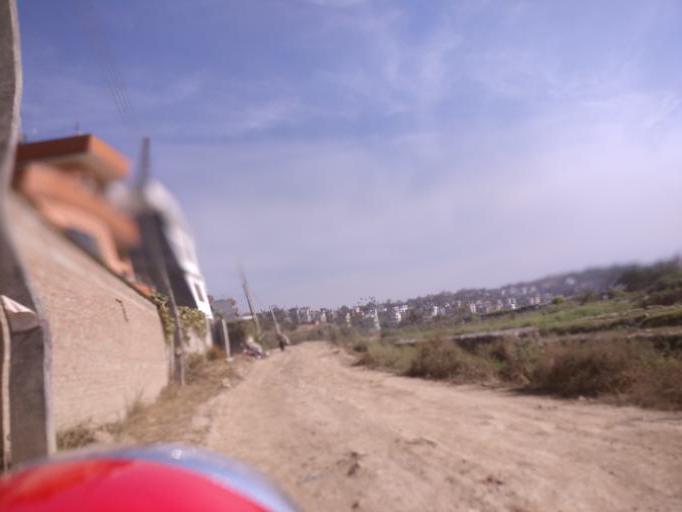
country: NP
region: Central Region
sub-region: Bagmati Zone
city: Patan
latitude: 27.6591
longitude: 85.3084
